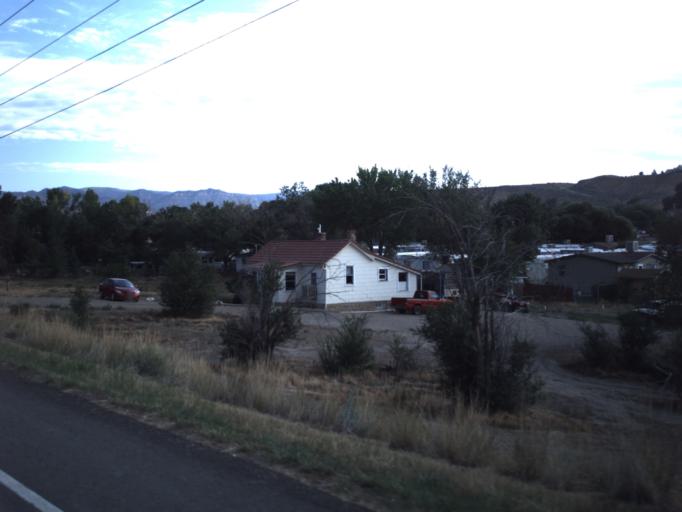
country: US
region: Utah
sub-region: Carbon County
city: Price
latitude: 39.5893
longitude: -110.7892
